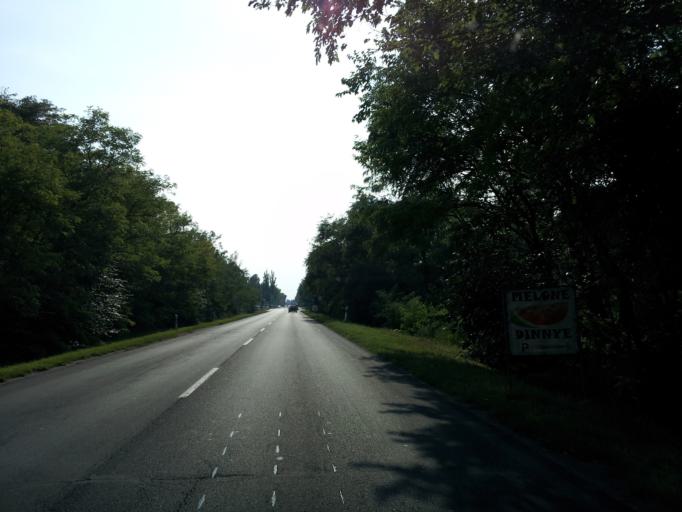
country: HU
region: Somogy
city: Siofok
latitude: 46.9207
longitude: 18.0908
